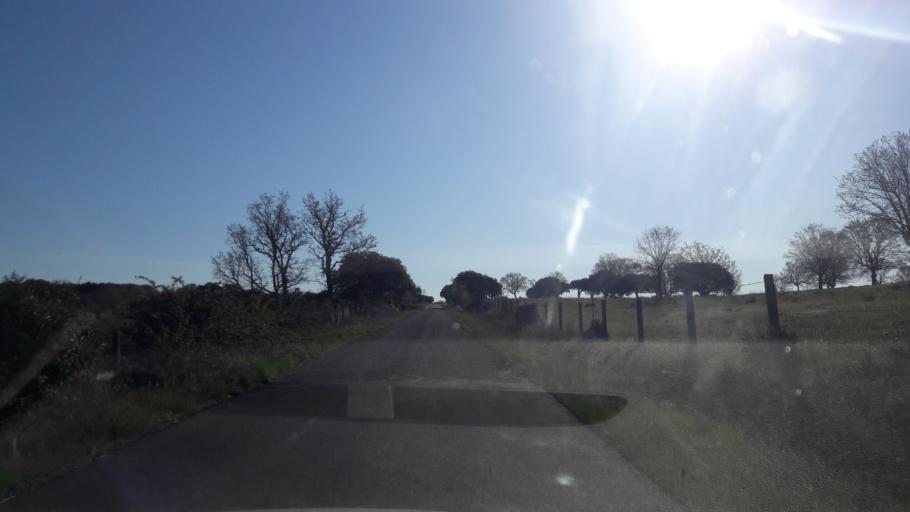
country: ES
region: Castille and Leon
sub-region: Provincia de Salamanca
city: Monleon
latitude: 40.6068
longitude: -5.8350
